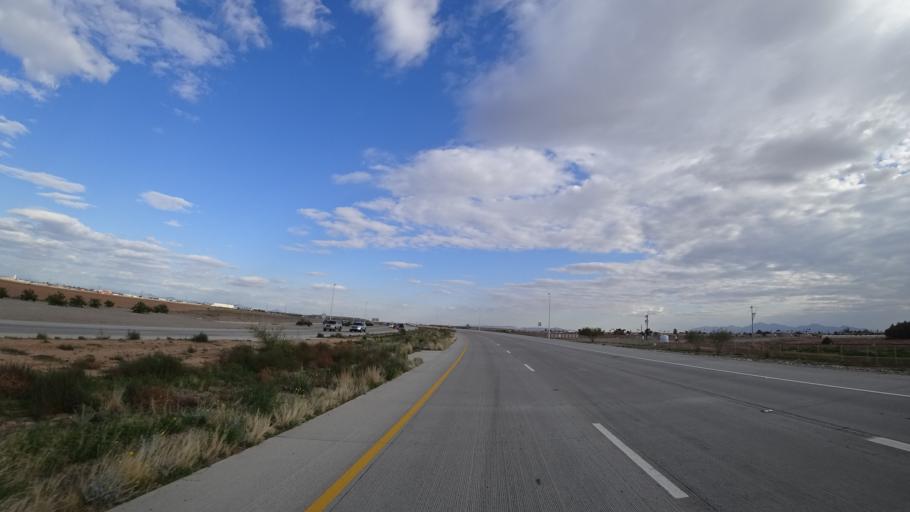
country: US
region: Arizona
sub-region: Maricopa County
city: Litchfield Park
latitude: 33.5524
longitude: -112.3511
